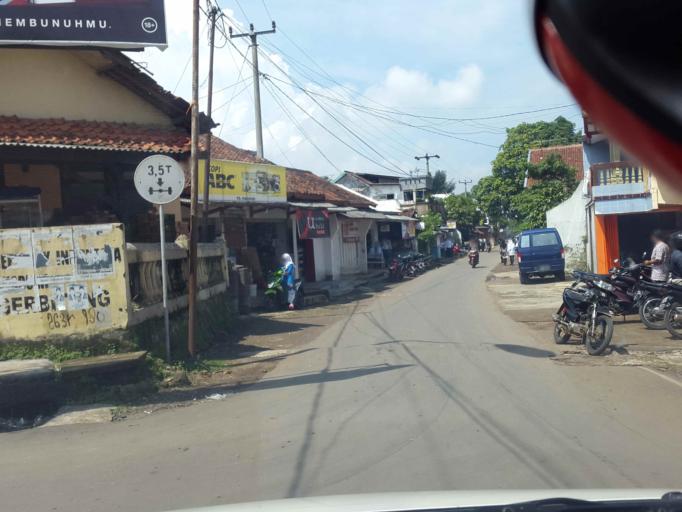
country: ID
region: West Java
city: Pasirreungit
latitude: -6.9825
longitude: 107.0263
